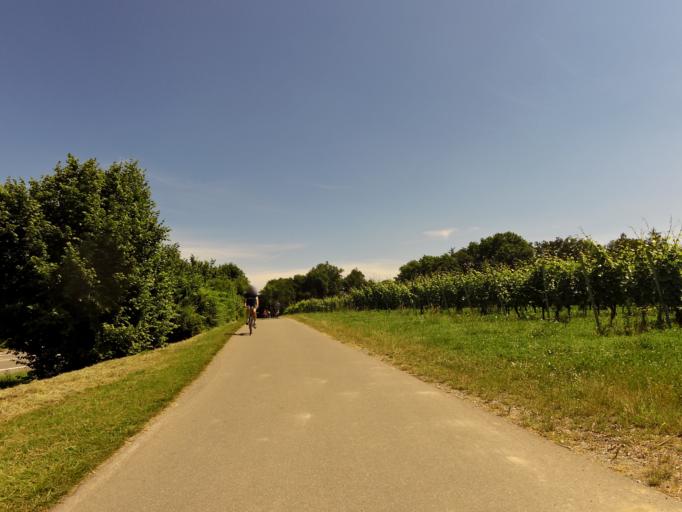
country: DE
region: Baden-Wuerttemberg
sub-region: Tuebingen Region
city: Hagnau
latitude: 47.6677
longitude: 9.3408
